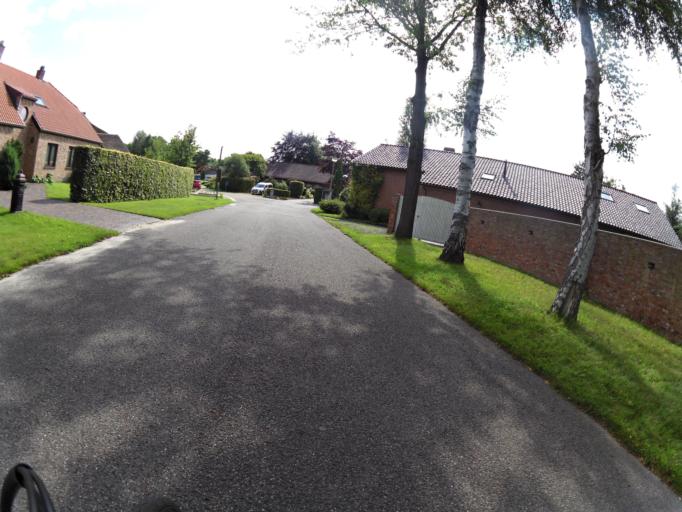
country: BE
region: Flanders
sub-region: Provincie Antwerpen
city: Balen
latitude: 51.1899
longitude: 5.2033
